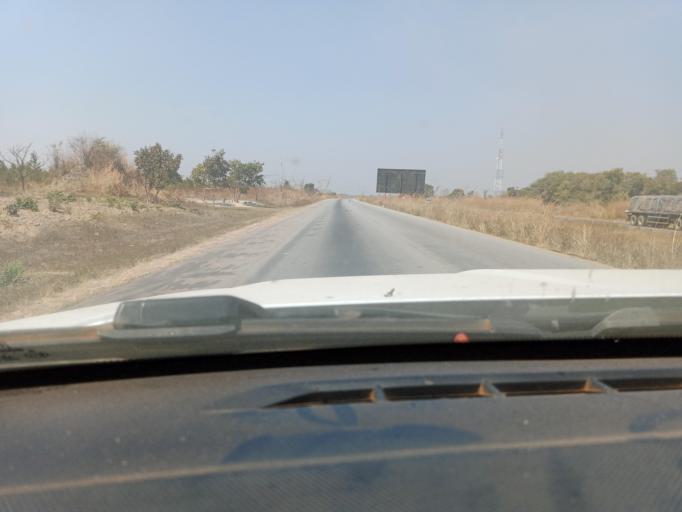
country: ZM
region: Copperbelt
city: Luanshya
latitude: -12.9472
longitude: 28.3801
